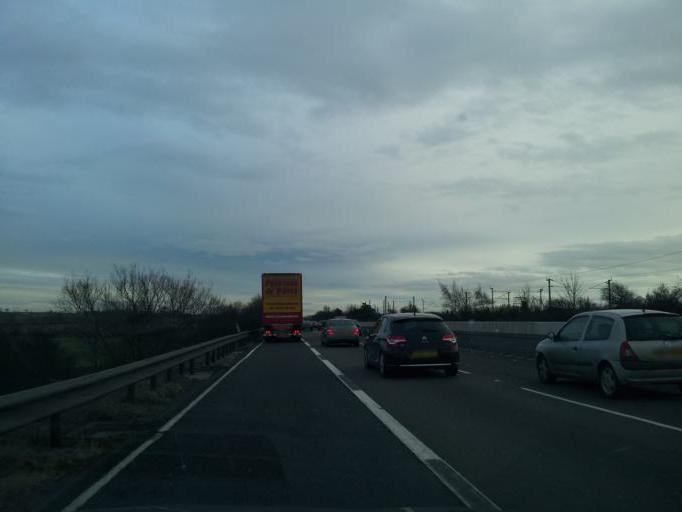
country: GB
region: England
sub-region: Northamptonshire
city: Long Buckby
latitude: 52.2892
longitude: -1.1058
